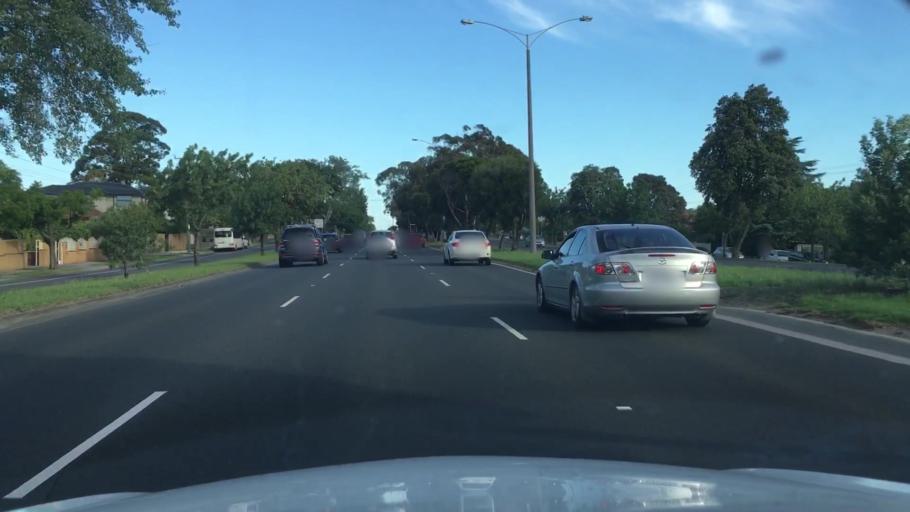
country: AU
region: Victoria
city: Clayton
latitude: -37.9018
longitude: 145.1073
